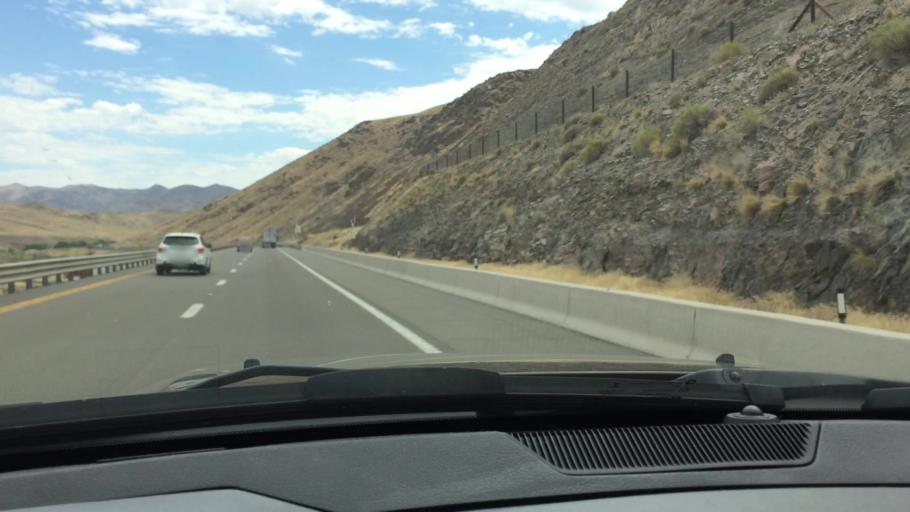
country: US
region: Nevada
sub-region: Lyon County
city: Fernley
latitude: 39.5811
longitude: -119.4706
